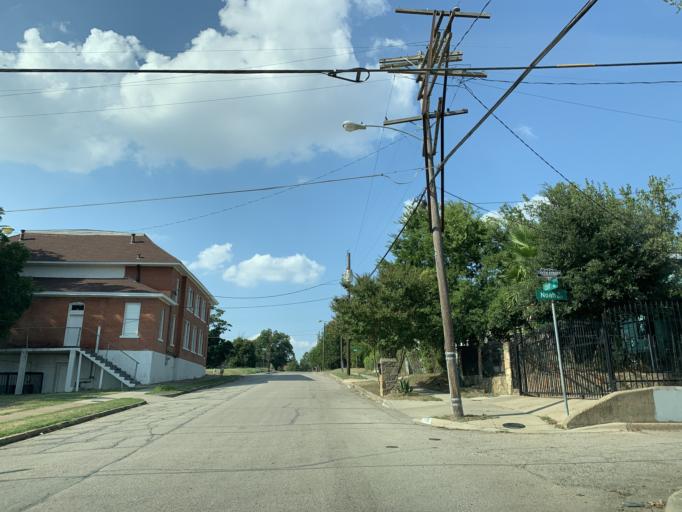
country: US
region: Texas
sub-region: Dallas County
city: Dallas
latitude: 32.7491
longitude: -96.8069
